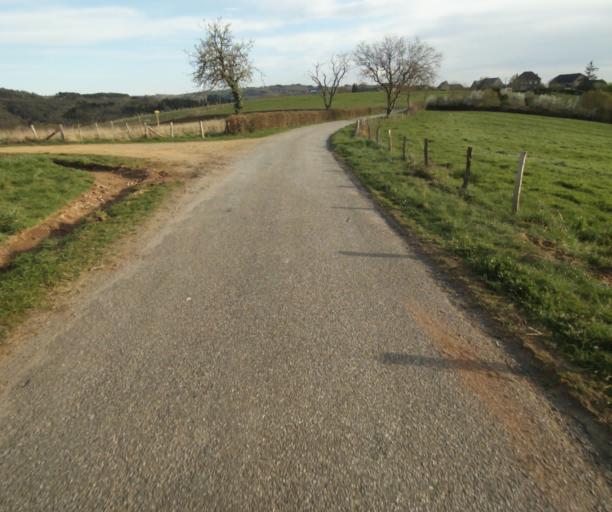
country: FR
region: Limousin
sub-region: Departement de la Correze
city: Correze
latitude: 45.3678
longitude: 1.8327
